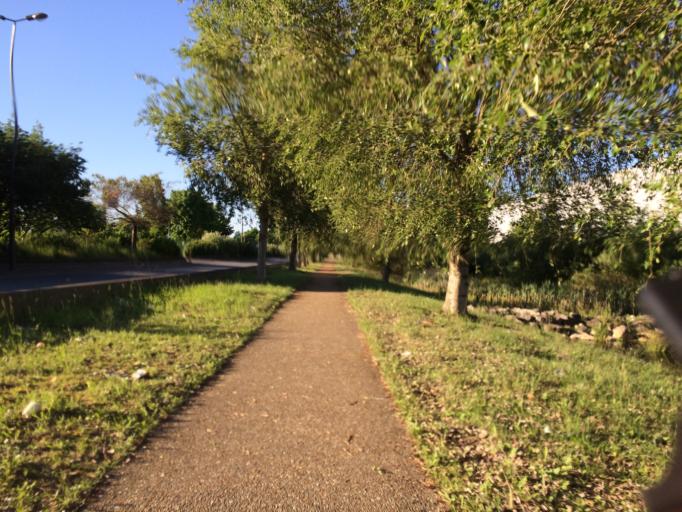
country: FR
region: Ile-de-France
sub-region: Departement de l'Essonne
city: Chilly-Mazarin
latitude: 48.7216
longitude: 2.3023
